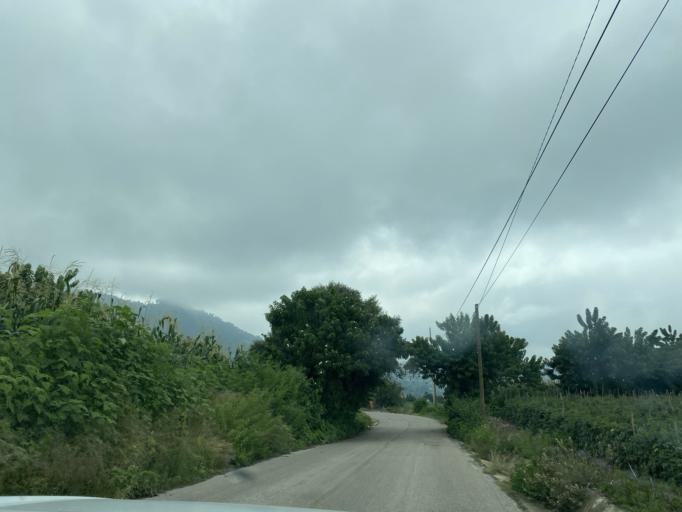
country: MX
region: Morelos
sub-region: Yecapixtla
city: Achichipico
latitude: 18.9556
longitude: -98.8312
